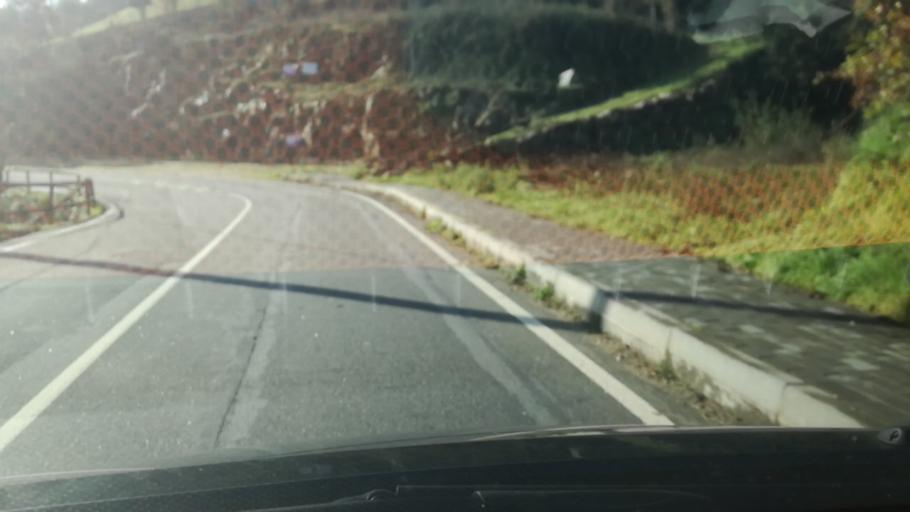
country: PT
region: Braga
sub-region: Guimaraes
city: Ponte
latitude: 41.5244
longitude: -8.3424
